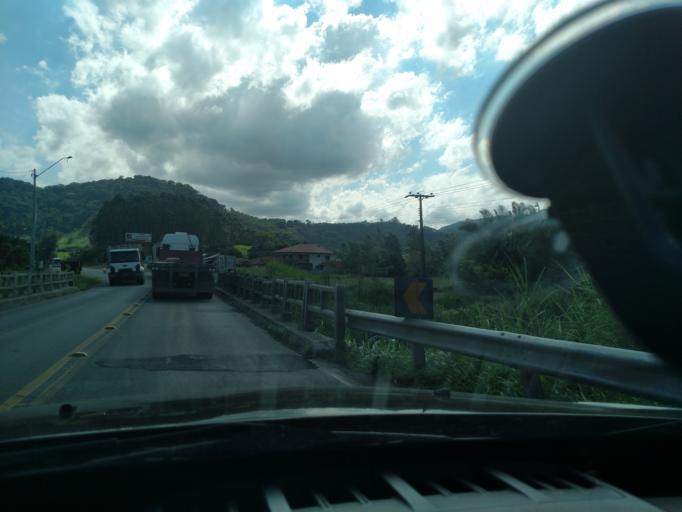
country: BR
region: Santa Catarina
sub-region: Rodeio
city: Gavea
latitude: -26.9482
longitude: -49.3186
